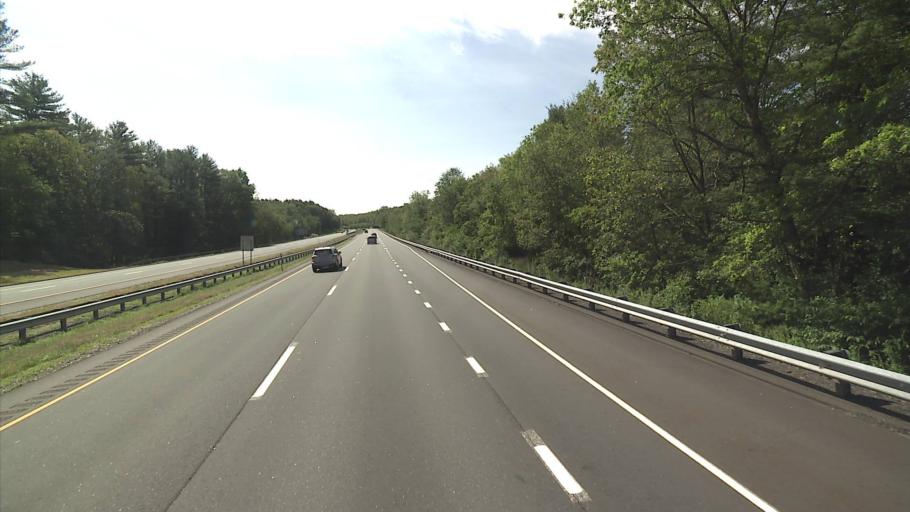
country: US
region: Connecticut
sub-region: Hartford County
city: Terramuggus
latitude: 41.5990
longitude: -72.4182
